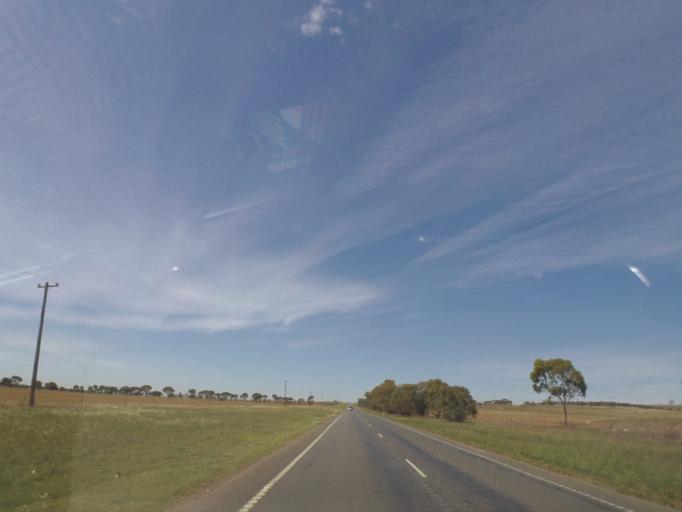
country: AU
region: Victoria
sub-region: Moorabool
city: Bacchus Marsh
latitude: -37.7637
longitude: 144.4404
